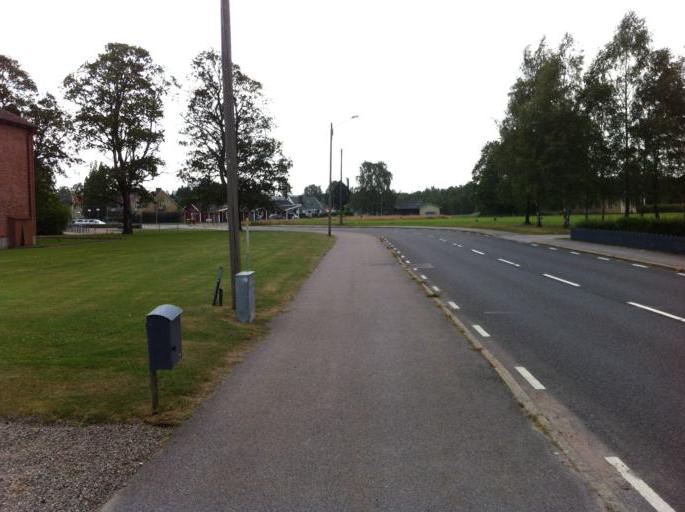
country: SE
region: Joenkoeping
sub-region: Gislaveds Kommun
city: Reftele
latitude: 56.9581
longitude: 13.5318
